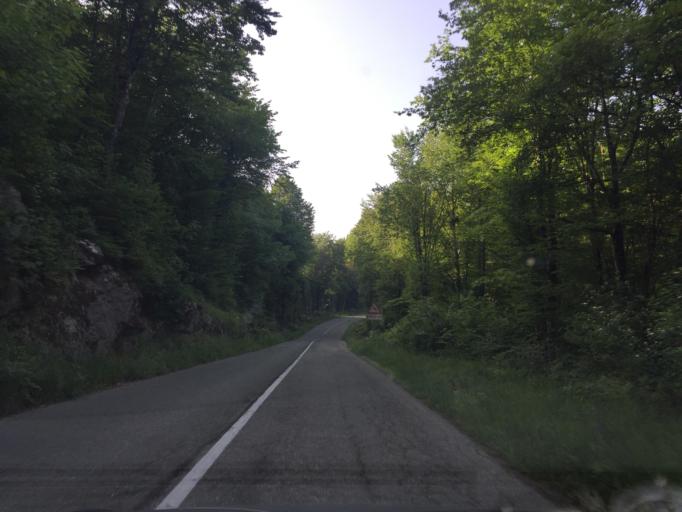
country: HR
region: Primorsko-Goranska
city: Matulji
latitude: 45.4226
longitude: 14.2250
